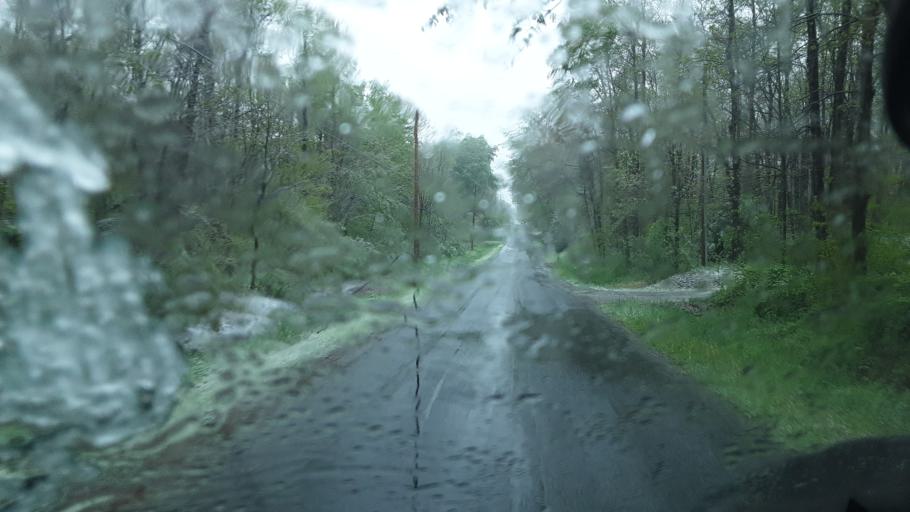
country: US
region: Ohio
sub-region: Portage County
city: Garrettsville
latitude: 41.3066
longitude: -81.0387
